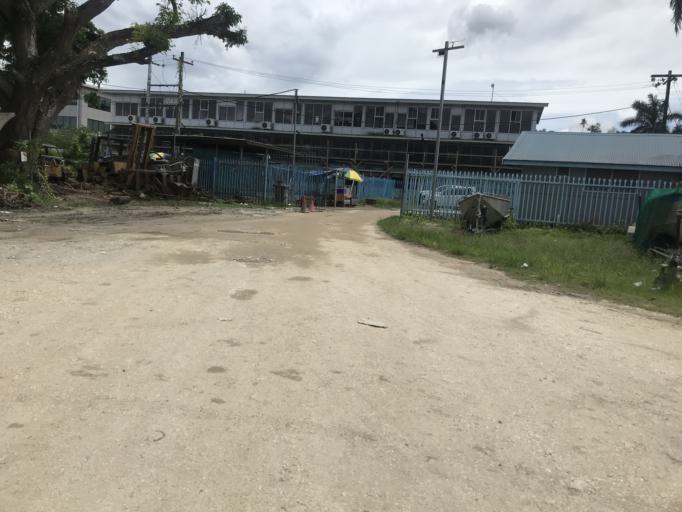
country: SB
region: Guadalcanal
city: Honiara
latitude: -9.4296
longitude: 159.9516
